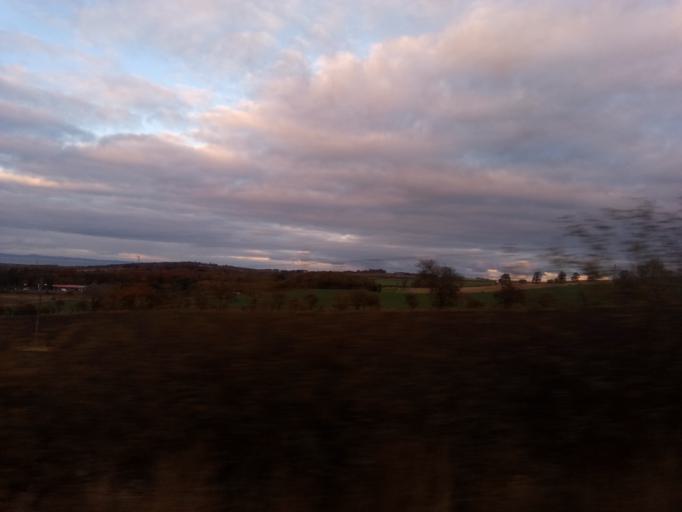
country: GB
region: Scotland
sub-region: Midlothian
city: Dalkeith
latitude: 55.8848
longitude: -3.0271
